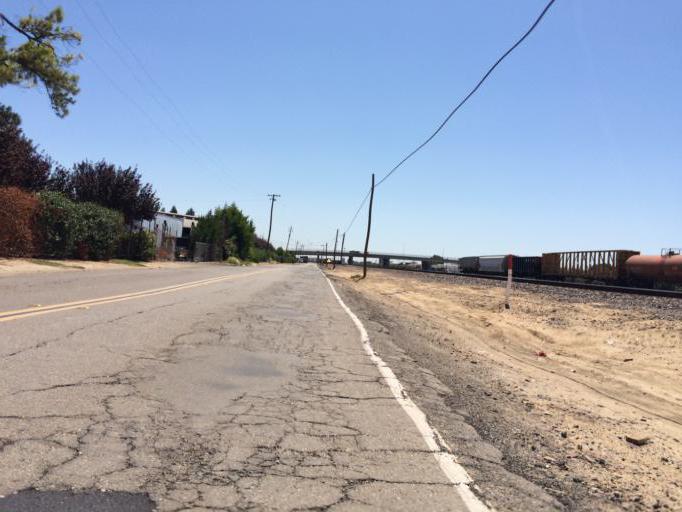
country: US
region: California
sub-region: Fresno County
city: Fresno
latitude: 36.7101
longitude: -119.7683
